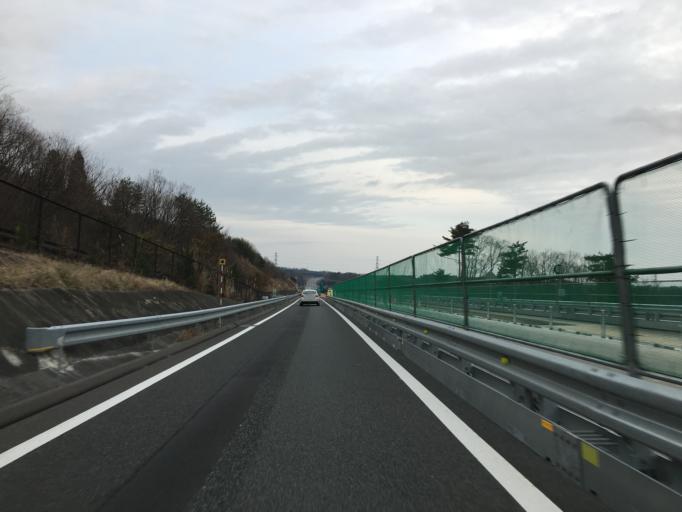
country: JP
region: Miyagi
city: Marumori
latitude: 37.8360
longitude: 140.8789
